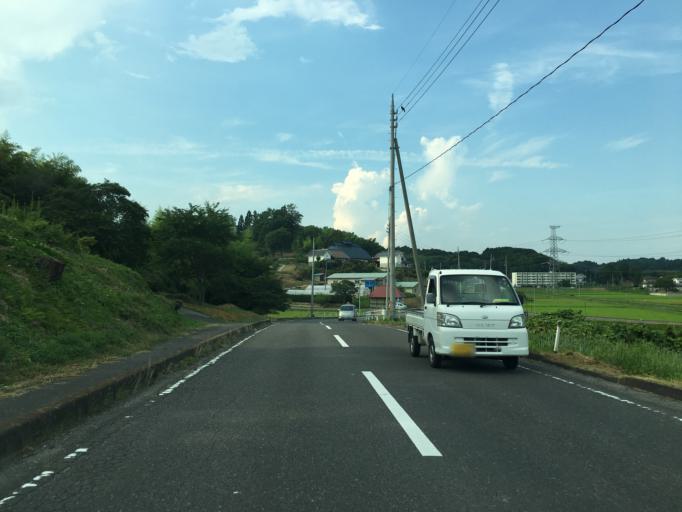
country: JP
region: Fukushima
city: Motomiya
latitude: 37.5015
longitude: 140.4328
